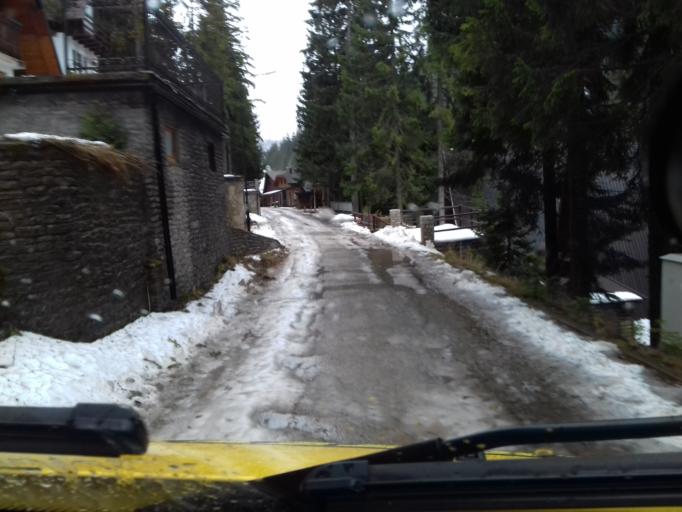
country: BA
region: Federation of Bosnia and Herzegovina
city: Turbe
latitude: 44.3076
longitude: 17.5767
